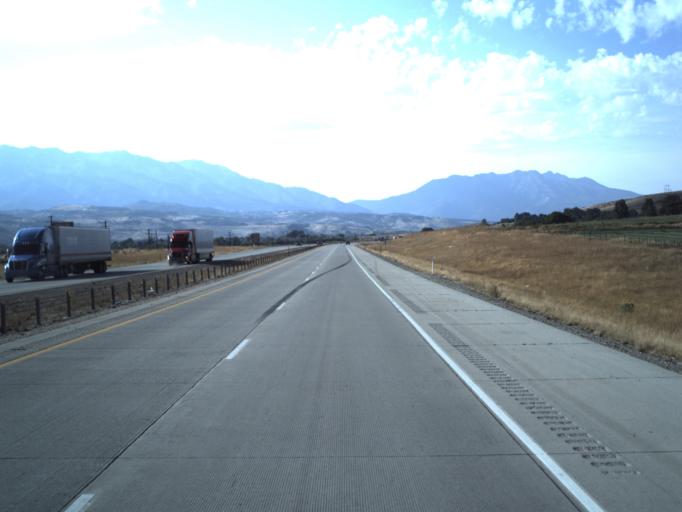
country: US
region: Utah
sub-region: Morgan County
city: Morgan
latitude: 41.0561
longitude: -111.6945
